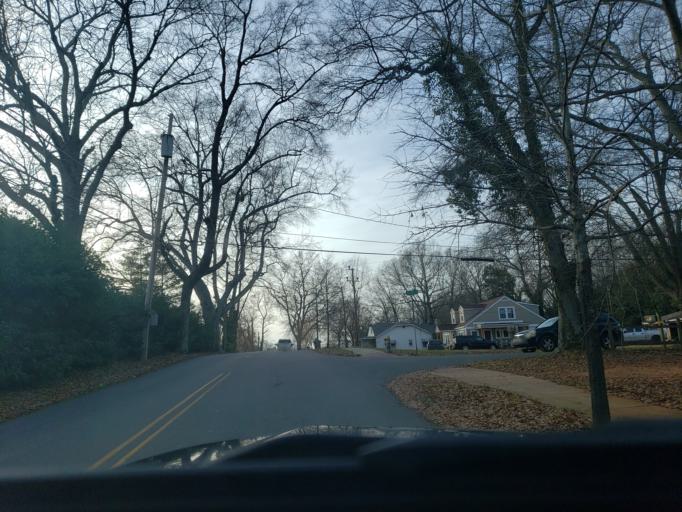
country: US
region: North Carolina
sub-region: Cleveland County
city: Shelby
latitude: 35.2892
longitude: -81.5278
